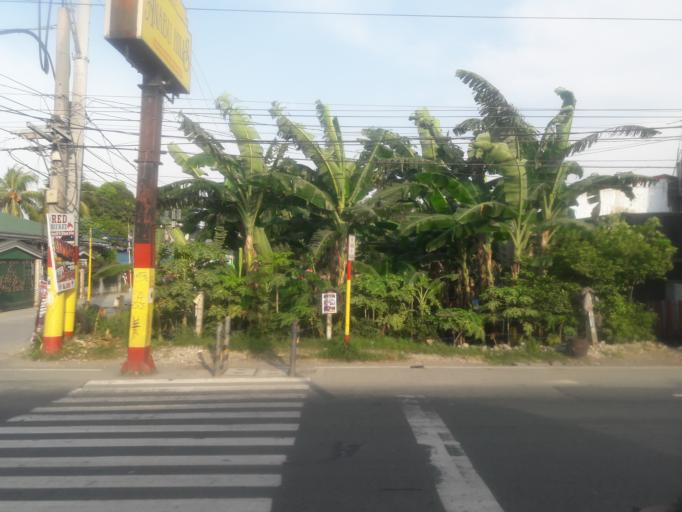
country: PH
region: Calabarzon
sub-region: Province of Cavite
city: Imus
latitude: 14.3942
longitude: 120.9399
